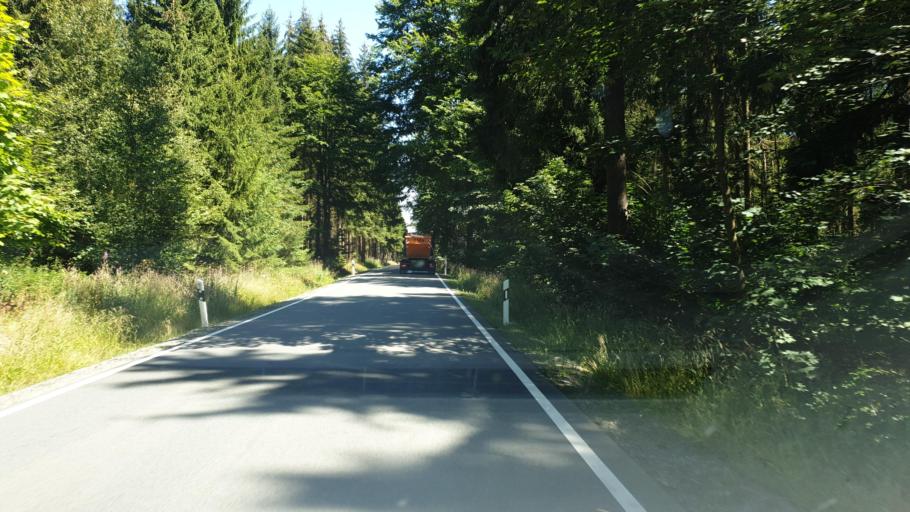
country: DE
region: Saxony
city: Bockau
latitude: 50.5100
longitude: 12.7274
